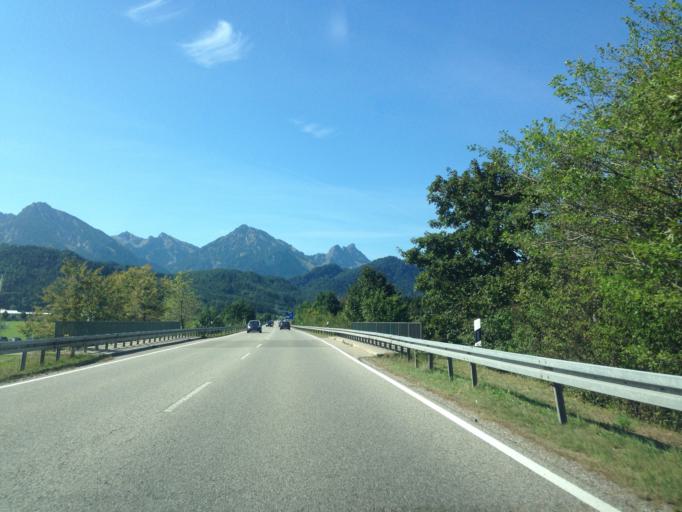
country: DE
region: Bavaria
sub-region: Swabia
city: Fuessen
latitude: 47.5778
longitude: 10.6727
